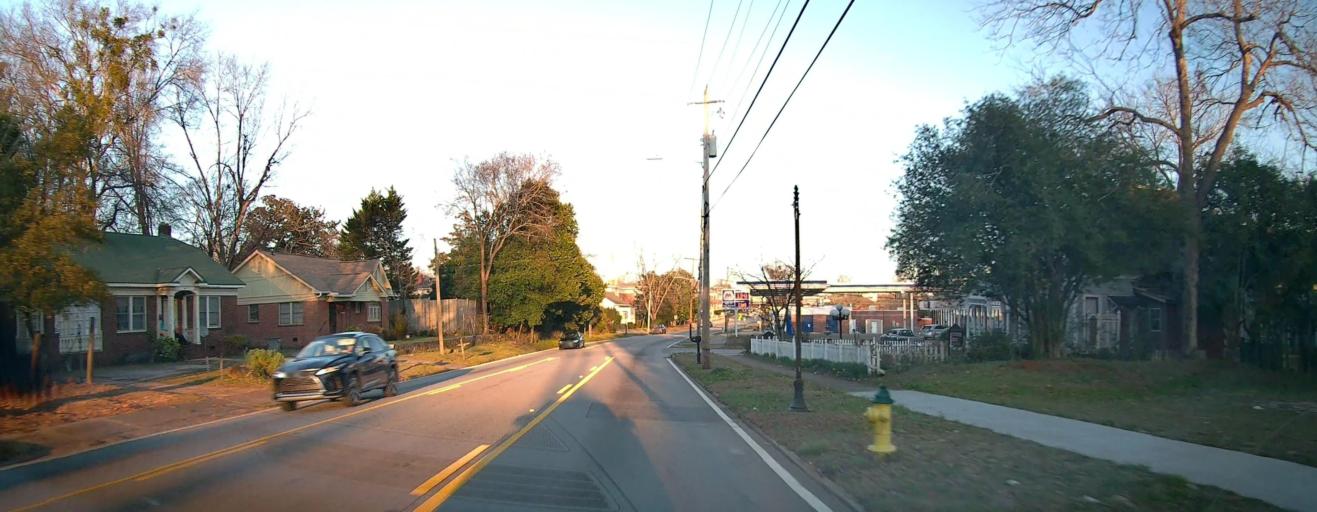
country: US
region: Georgia
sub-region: Troup County
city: La Grange
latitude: 33.0385
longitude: -85.0402
